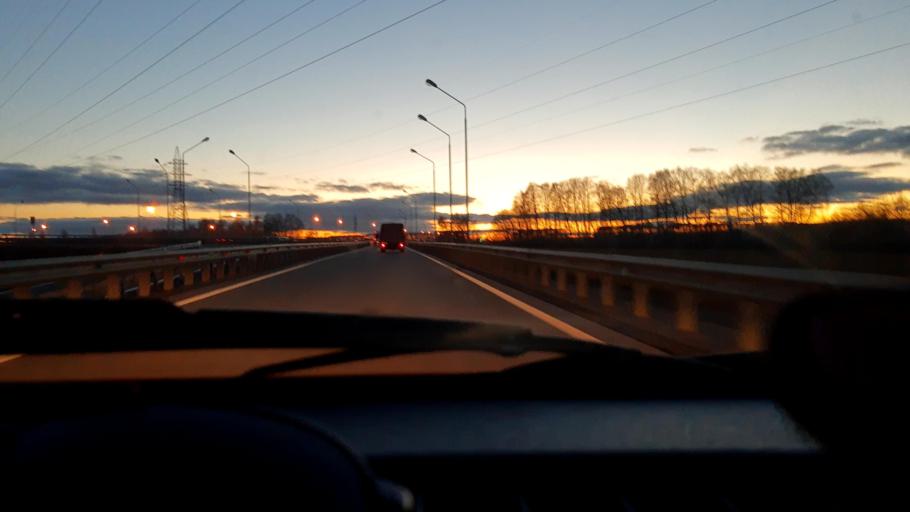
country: RU
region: Bashkortostan
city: Avdon
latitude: 54.6776
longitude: 55.8033
